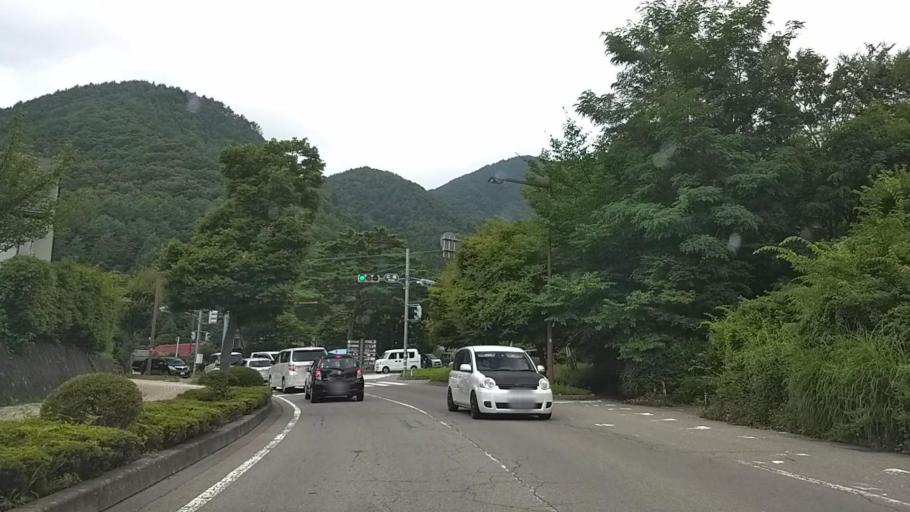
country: JP
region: Yamanashi
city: Fujikawaguchiko
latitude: 35.5256
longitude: 138.7618
